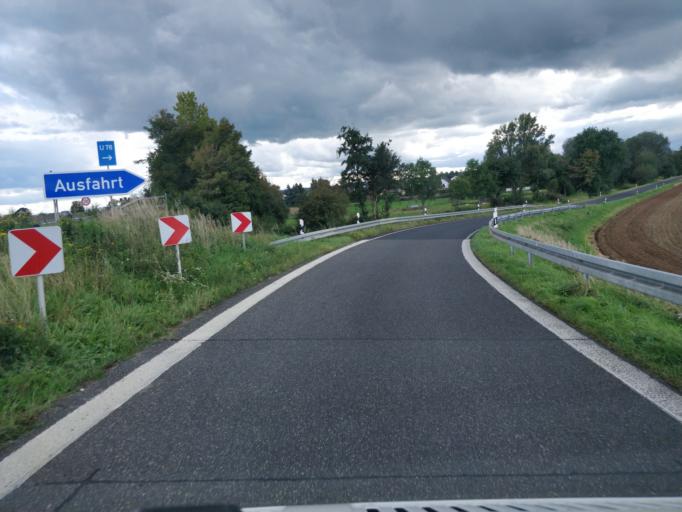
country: DE
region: North Rhine-Westphalia
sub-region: Regierungsbezirk Koln
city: Rheinbach
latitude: 50.6772
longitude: 6.9166
